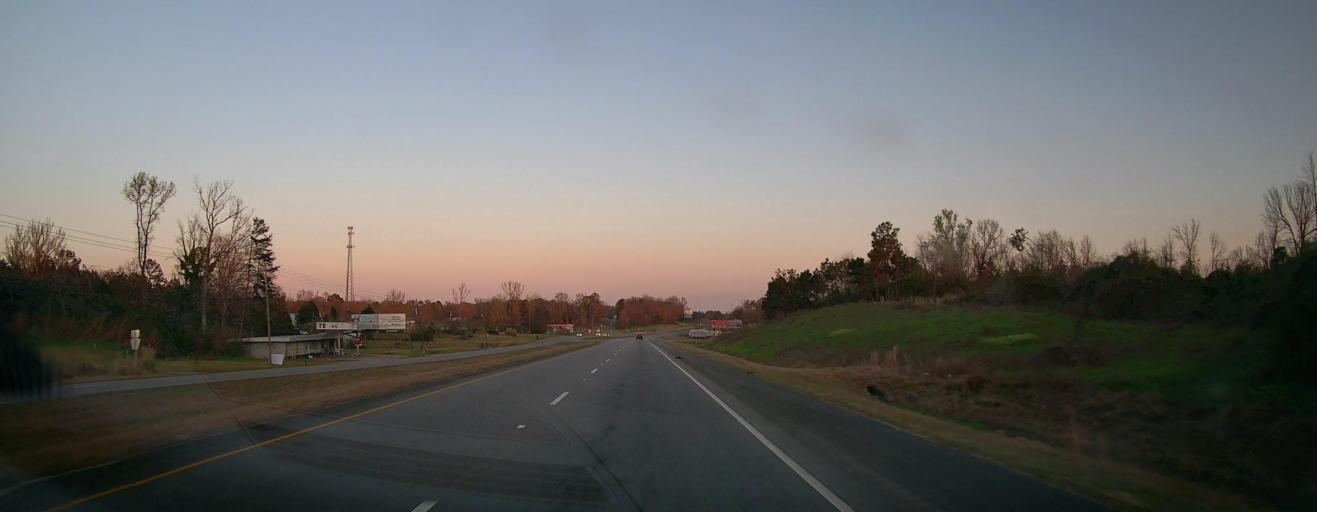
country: US
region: Alabama
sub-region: Tallapoosa County
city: Alexander City
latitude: 32.9705
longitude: -86.0153
